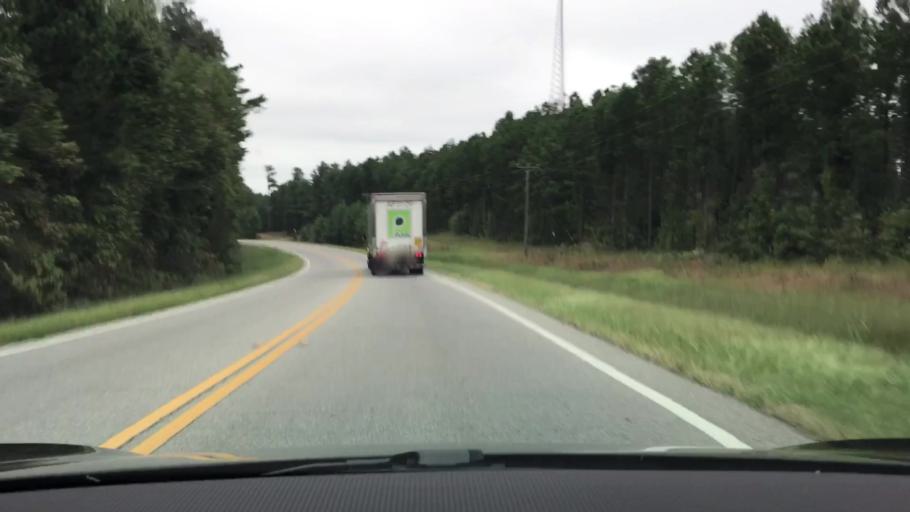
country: US
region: Georgia
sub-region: Greene County
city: Greensboro
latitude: 33.6625
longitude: -83.2436
